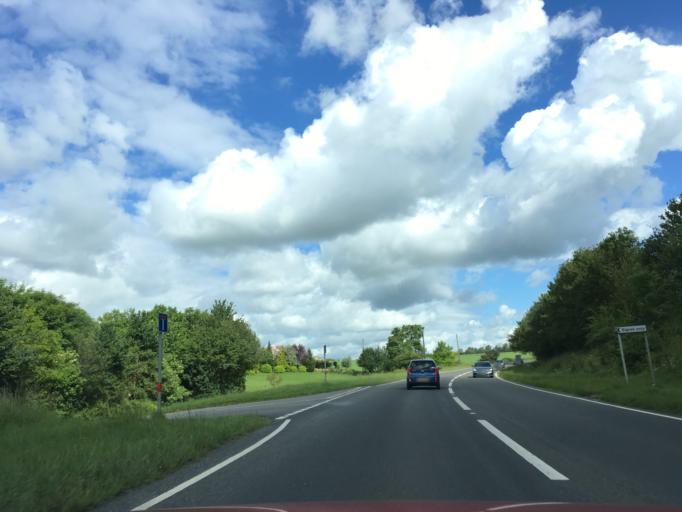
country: GB
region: England
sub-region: Oxfordshire
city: Burford
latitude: 51.7910
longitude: -1.6438
